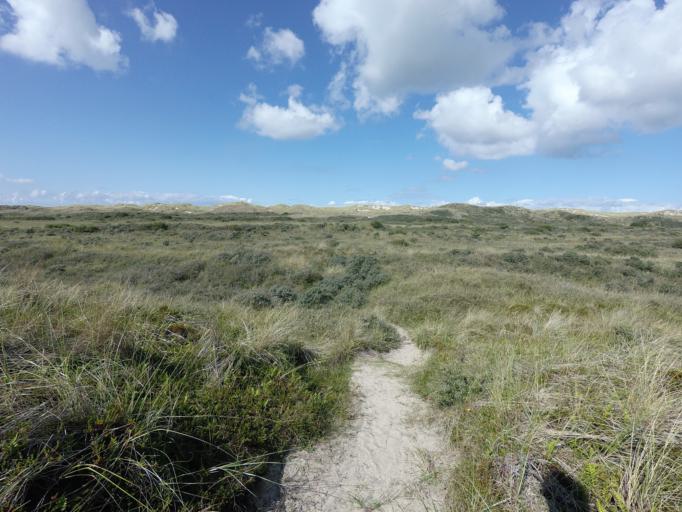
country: NL
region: Friesland
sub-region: Gemeente Terschelling
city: West-Terschelling
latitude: 53.3875
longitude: 5.2038
